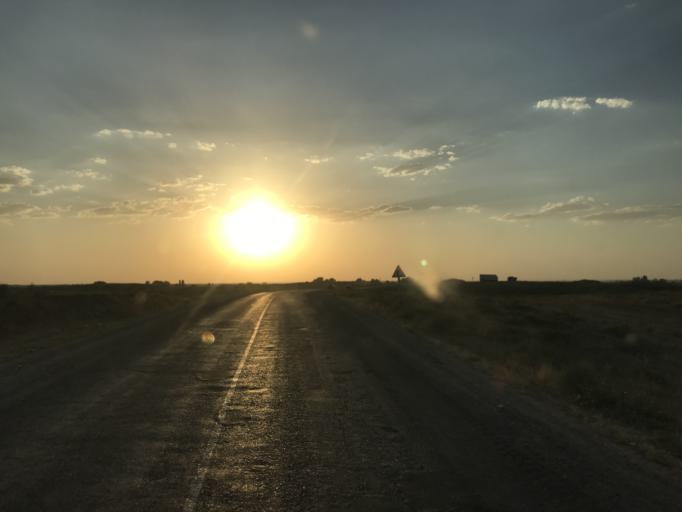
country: UZ
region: Toshkent
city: Yangiyul
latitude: 41.3374
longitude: 68.8815
